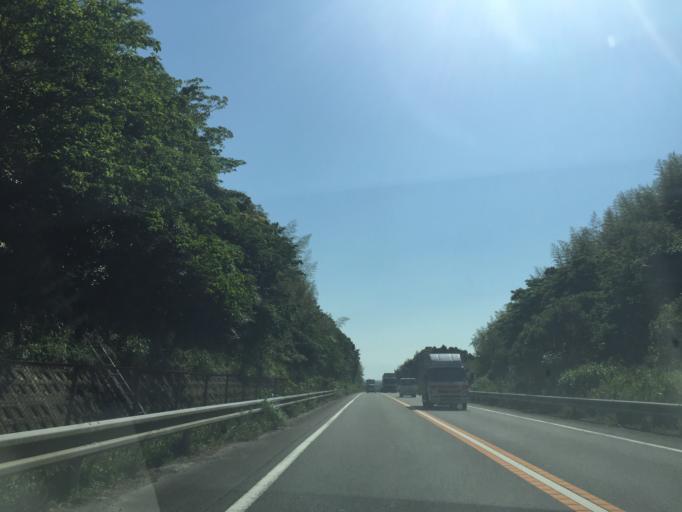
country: JP
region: Shizuoka
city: Kakegawa
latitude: 34.7848
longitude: 138.0054
